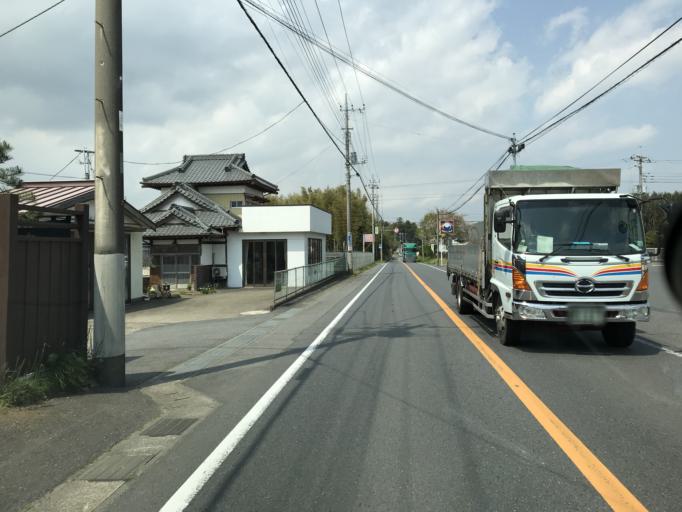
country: JP
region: Chiba
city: Sawara
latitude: 35.8623
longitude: 140.5483
